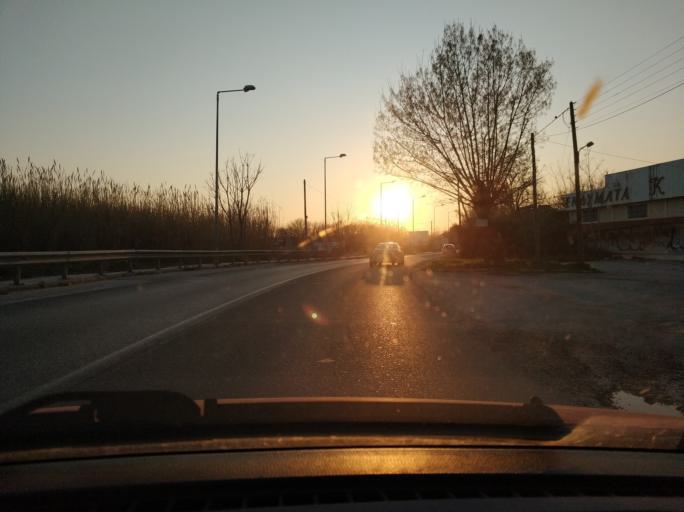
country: GR
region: Central Macedonia
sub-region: Nomos Thessalonikis
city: Lagkadas
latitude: 40.7457
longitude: 23.0692
